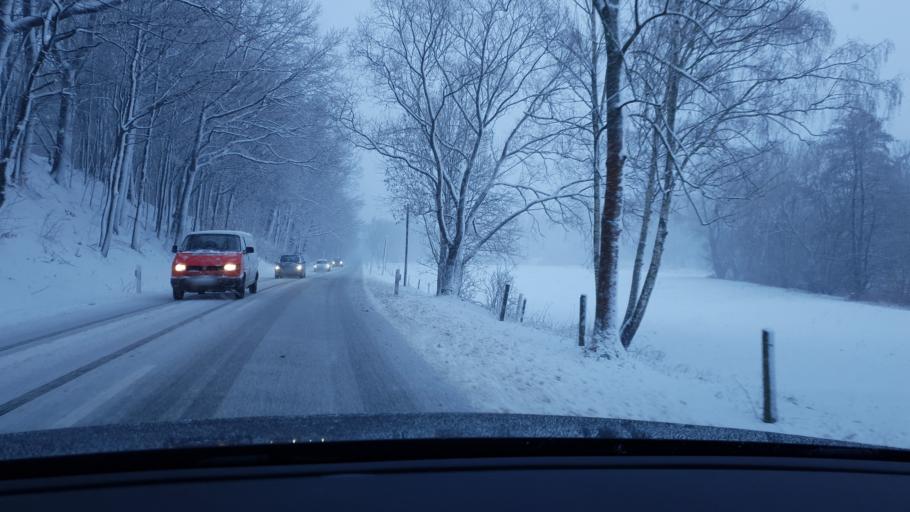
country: DE
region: Saxony
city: Claussnitz
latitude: 50.9138
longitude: 12.8996
